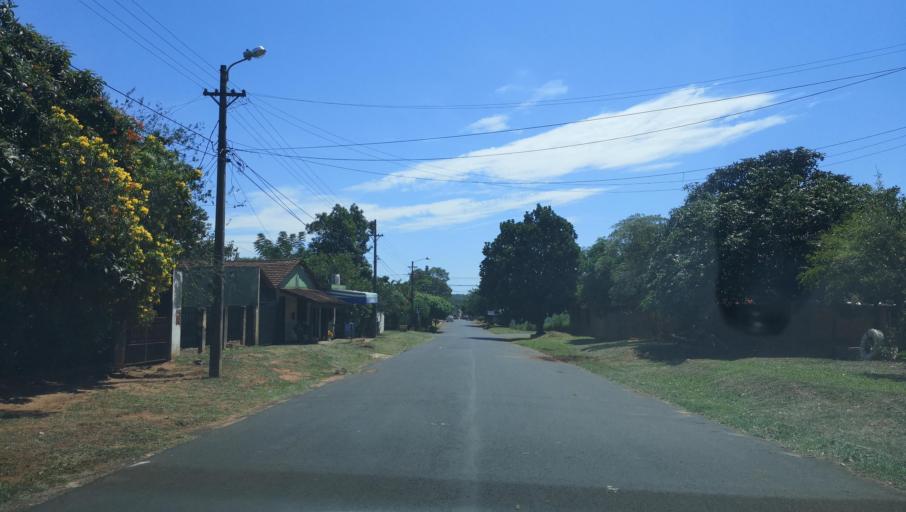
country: PY
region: Misiones
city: Santa Maria
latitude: -26.8924
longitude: -57.0297
